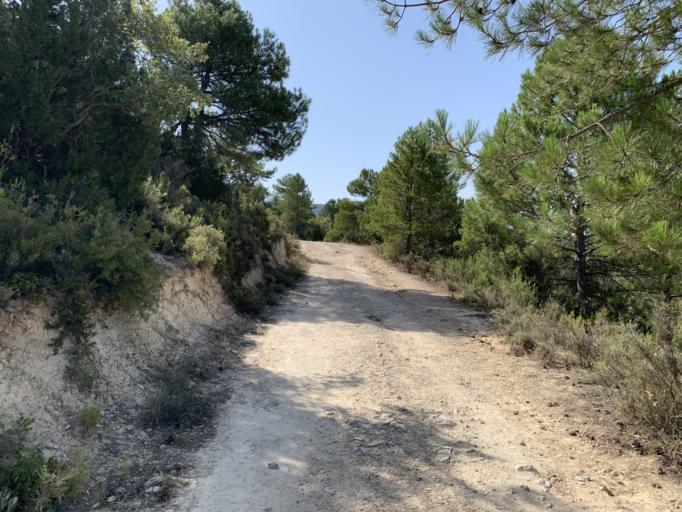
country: ES
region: Castille-La Mancha
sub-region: Provincia de Guadalajara
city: Ocentejo
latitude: 40.7637
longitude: -2.3915
